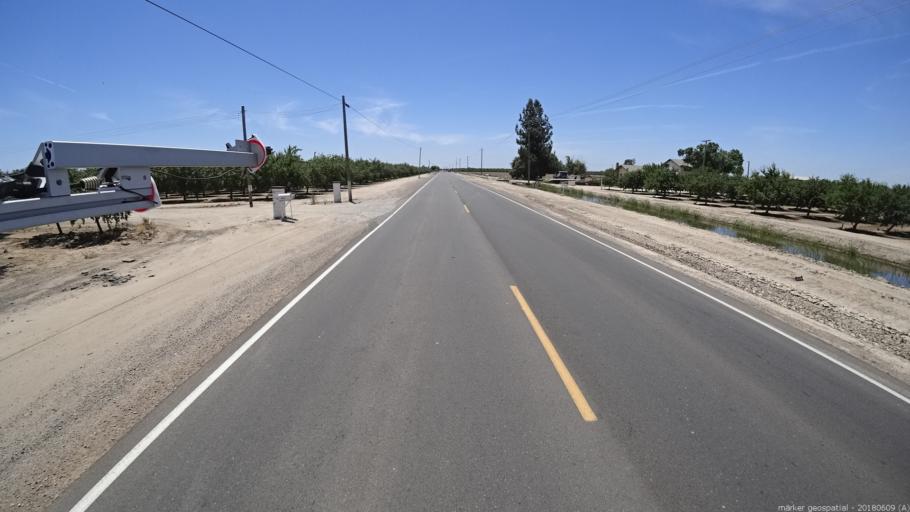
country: US
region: California
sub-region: Madera County
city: Parkwood
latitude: 36.9279
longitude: -120.0742
